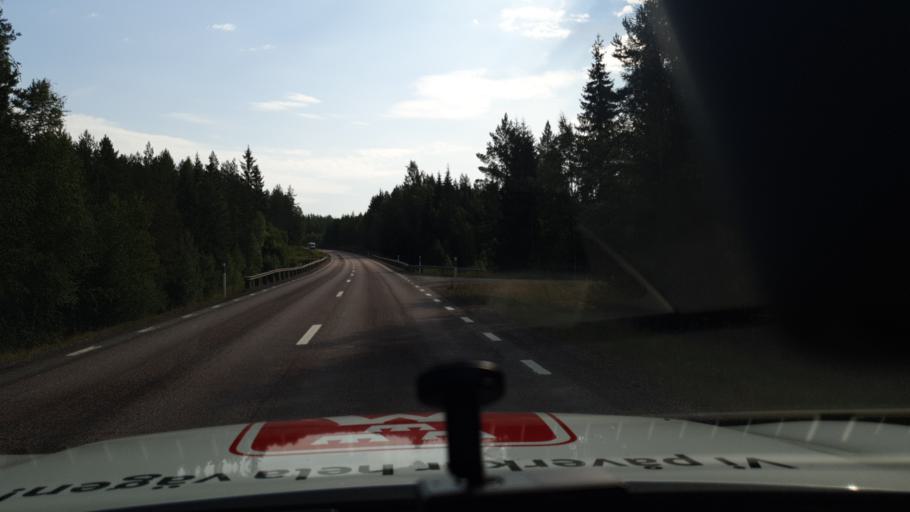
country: SE
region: Vaermland
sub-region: Hagfors Kommun
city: Ekshaerad
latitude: 60.4791
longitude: 13.3288
